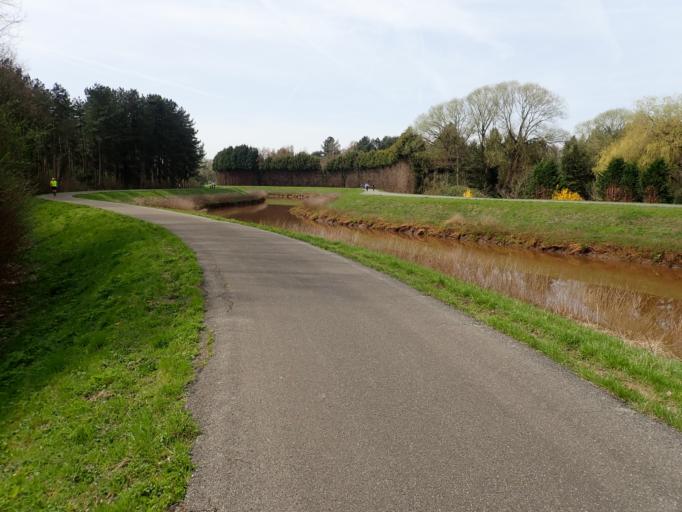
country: BE
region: Flanders
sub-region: Provincie Antwerpen
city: Nijlen
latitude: 51.1658
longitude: 4.6253
